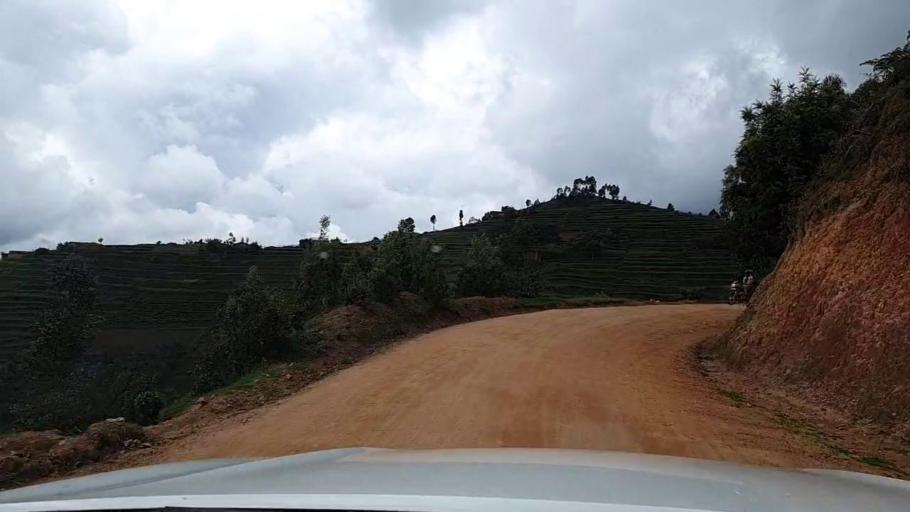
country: RW
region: Southern Province
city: Nzega
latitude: -2.4296
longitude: 29.4371
